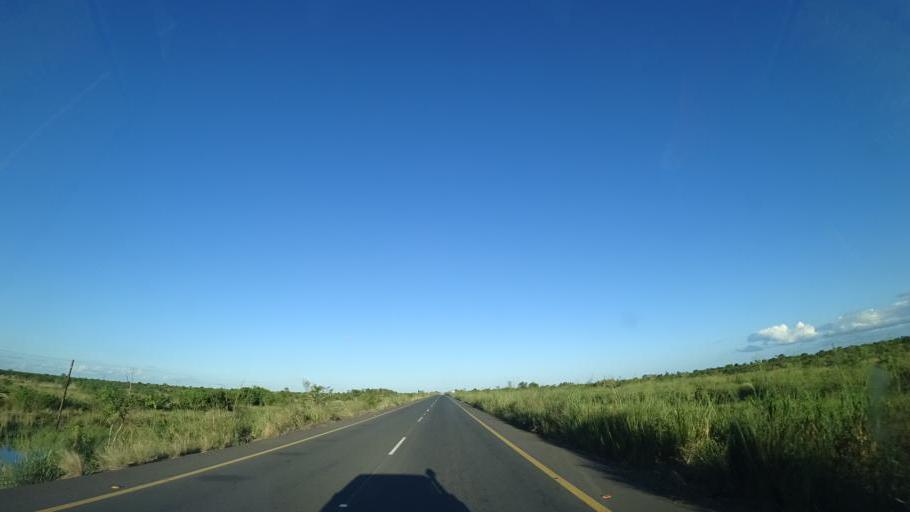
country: MZ
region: Sofala
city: Dondo
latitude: -19.3106
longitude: 34.2724
